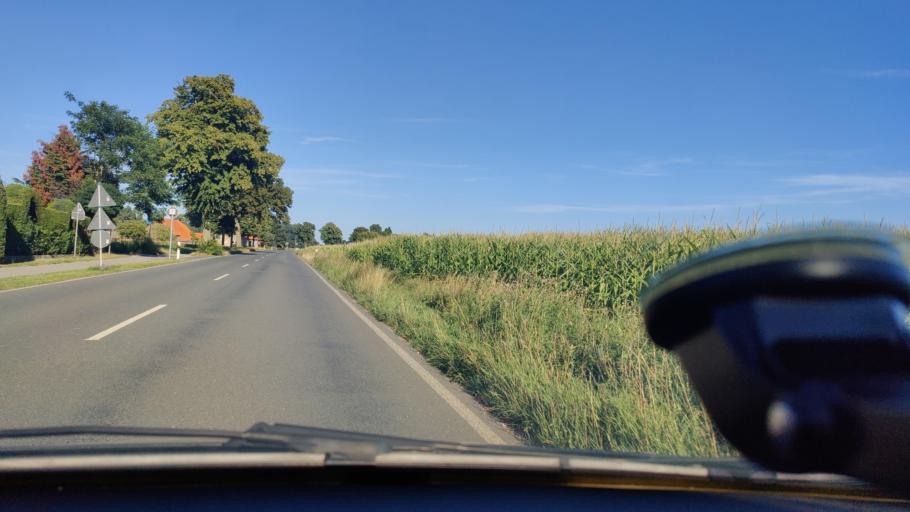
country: DE
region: North Rhine-Westphalia
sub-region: Regierungsbezirk Dusseldorf
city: Goch
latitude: 51.6750
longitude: 6.1256
